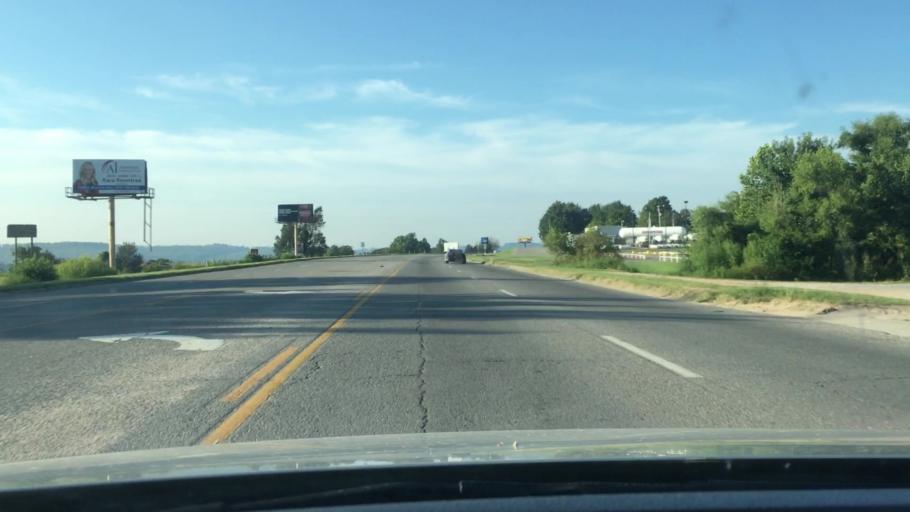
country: US
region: Oklahoma
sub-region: Cherokee County
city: Park Hill
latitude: 35.8659
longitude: -94.9763
